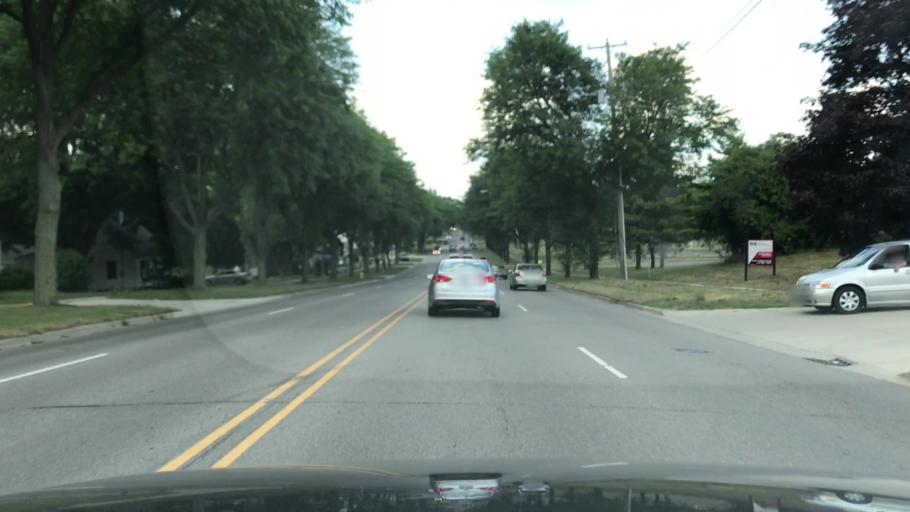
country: US
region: Michigan
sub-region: Kent County
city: Grand Rapids
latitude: 42.9862
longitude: -85.6398
